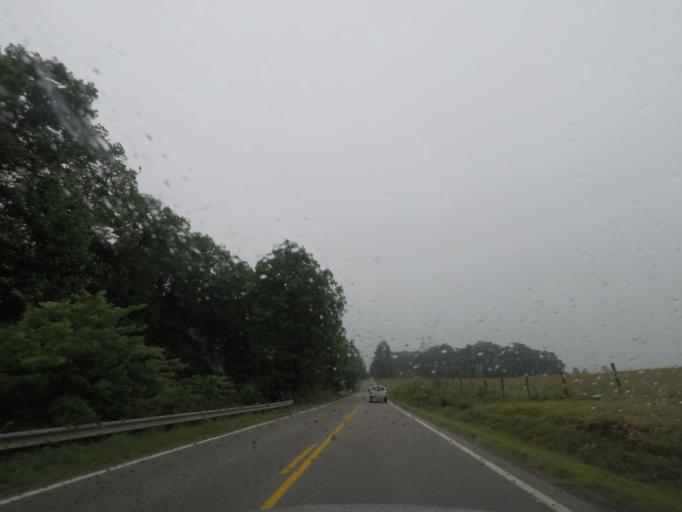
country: US
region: Virginia
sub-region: Prince Edward County
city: Farmville
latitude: 37.3264
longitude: -78.4647
